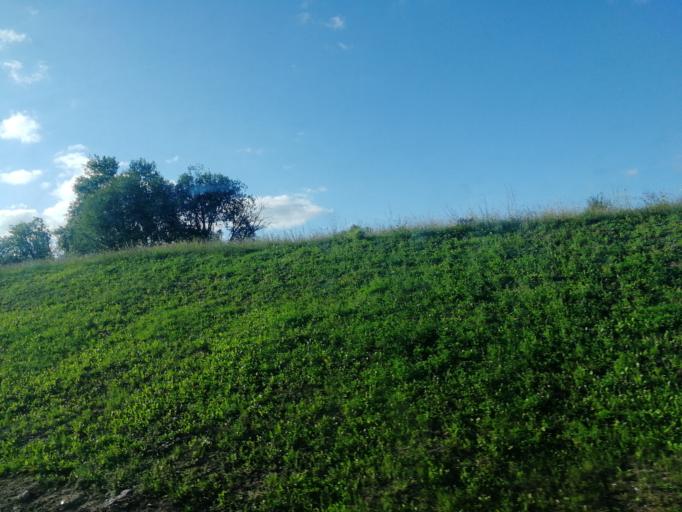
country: RU
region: Tula
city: Dubna
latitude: 54.2815
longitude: 37.1687
